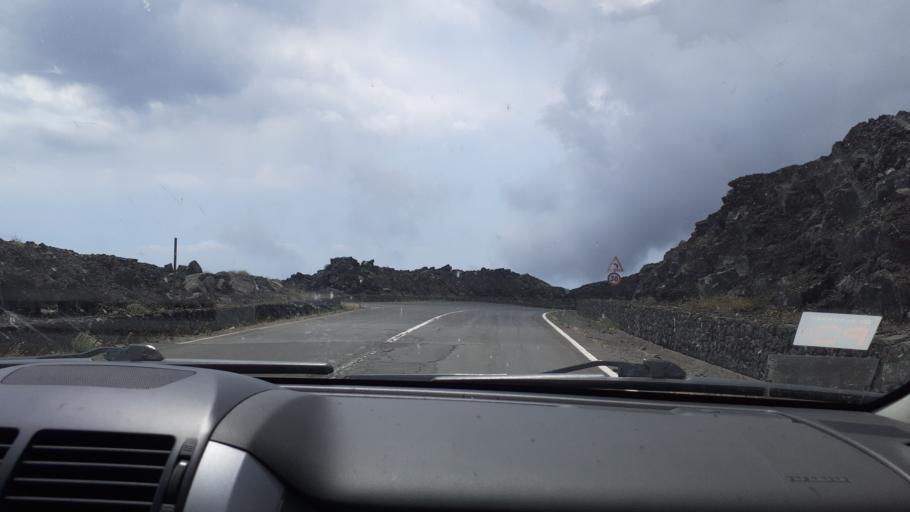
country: IT
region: Sicily
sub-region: Catania
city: Nicolosi
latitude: 37.6879
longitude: 15.0187
